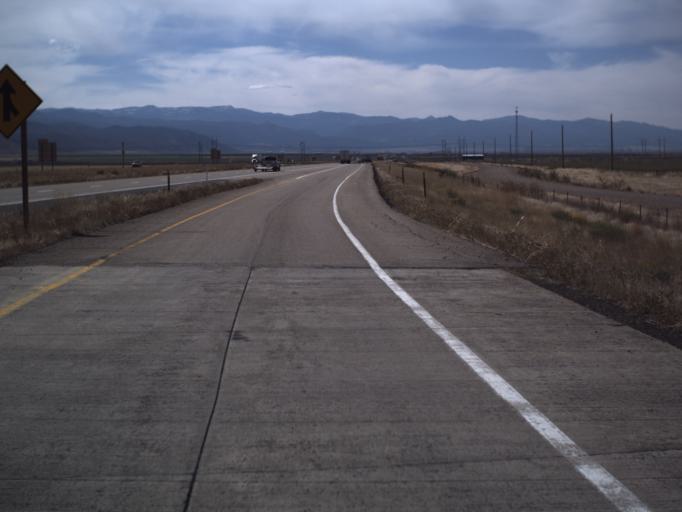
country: US
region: Utah
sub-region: Beaver County
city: Beaver
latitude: 38.0692
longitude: -112.6905
